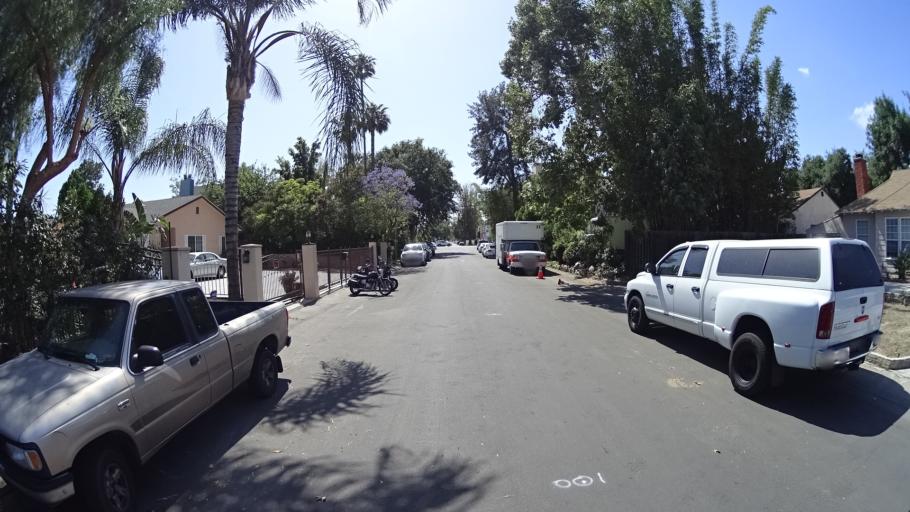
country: US
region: California
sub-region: Los Angeles County
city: North Hollywood
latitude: 34.1774
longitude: -118.3951
